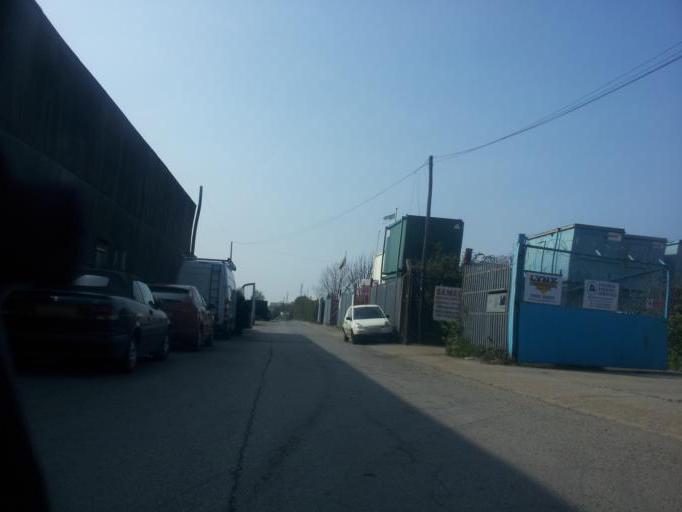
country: GB
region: England
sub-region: Kent
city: Gravesend
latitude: 51.4421
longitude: 0.3917
